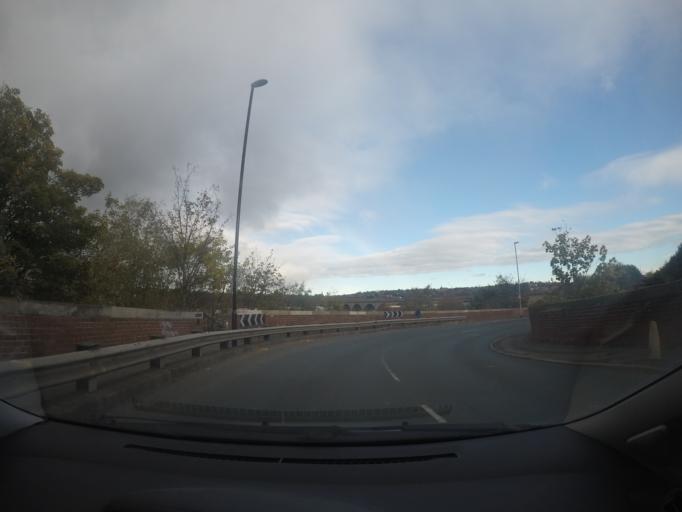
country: GB
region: England
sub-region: City and Borough of Leeds
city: Leeds
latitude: 53.8022
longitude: -1.5805
